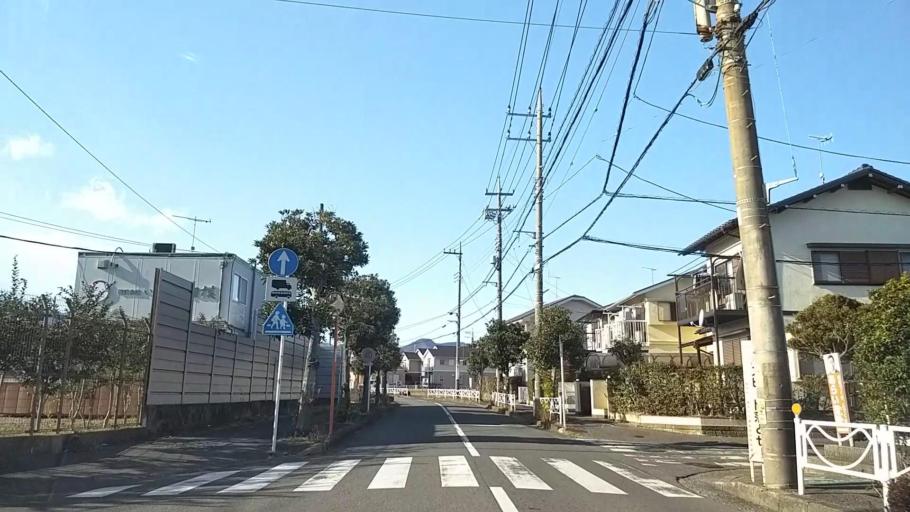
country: JP
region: Kanagawa
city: Atsugi
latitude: 35.4617
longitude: 139.3289
